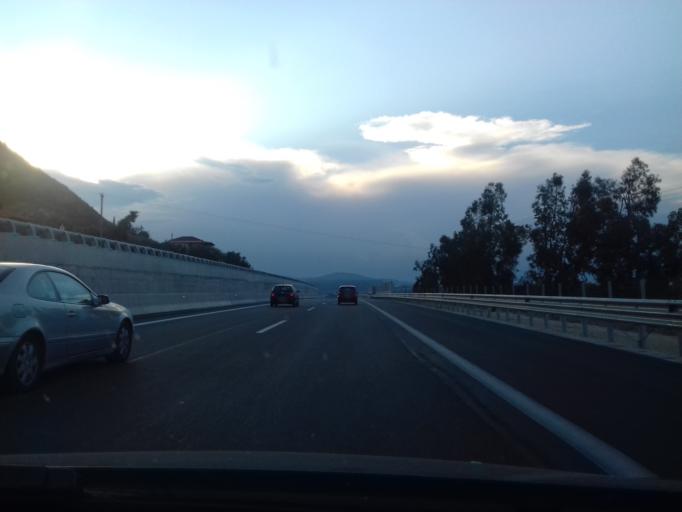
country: GR
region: West Greece
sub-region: Nomos Achaias
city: Temeni
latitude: 38.2120
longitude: 22.1249
